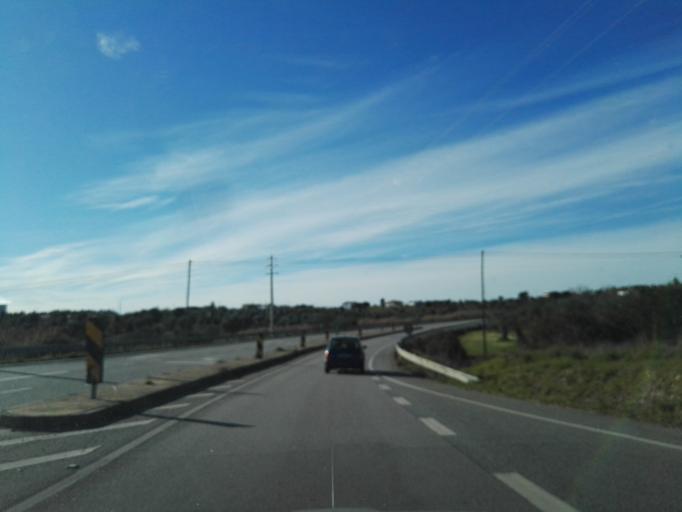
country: PT
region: Santarem
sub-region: Abrantes
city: Alferrarede
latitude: 39.4762
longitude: -8.0817
